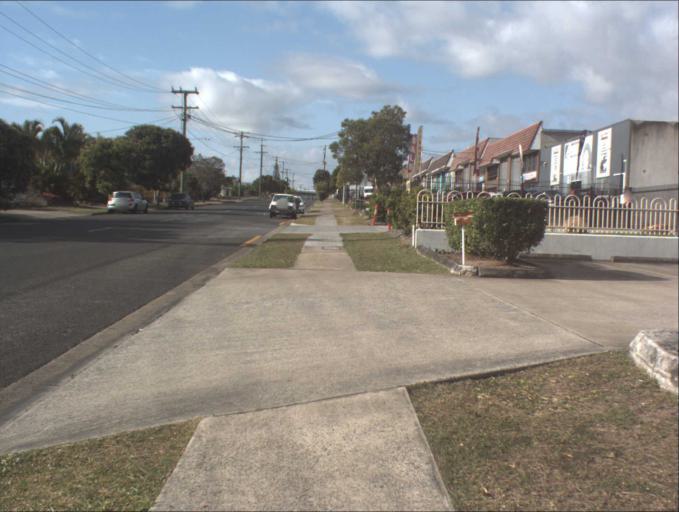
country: AU
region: Queensland
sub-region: Logan
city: Springwood
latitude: -27.6164
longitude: 153.1188
